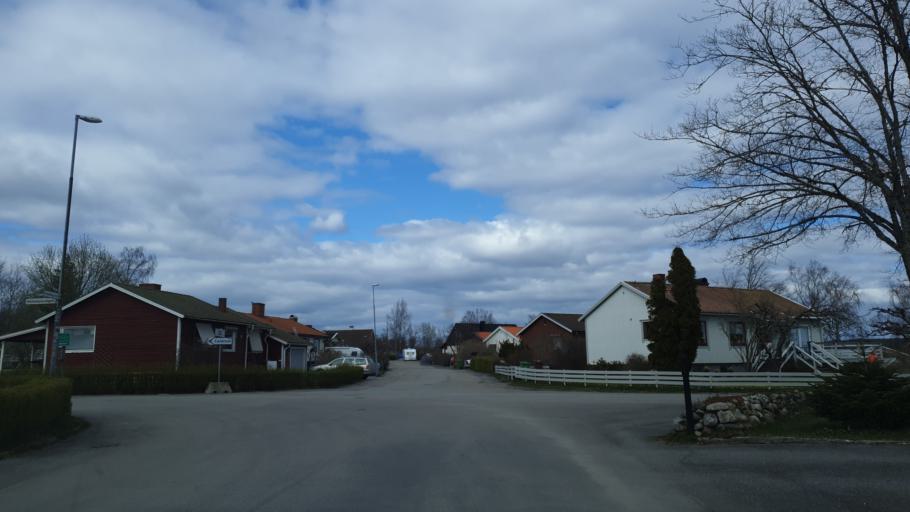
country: SE
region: OErebro
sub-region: Nora Kommun
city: Nora
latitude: 59.5279
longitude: 15.0405
